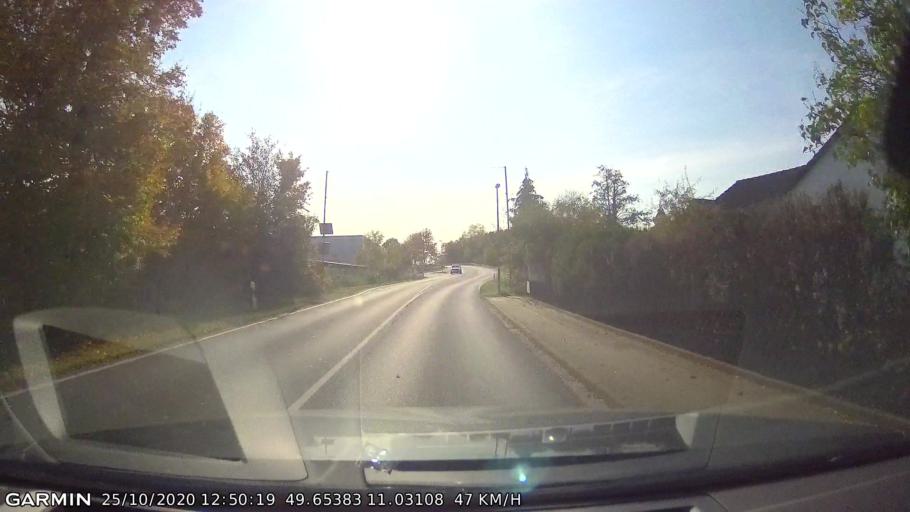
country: DE
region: Bavaria
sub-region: Regierungsbezirk Mittelfranken
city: Baiersdorf
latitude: 49.6536
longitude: 11.0310
